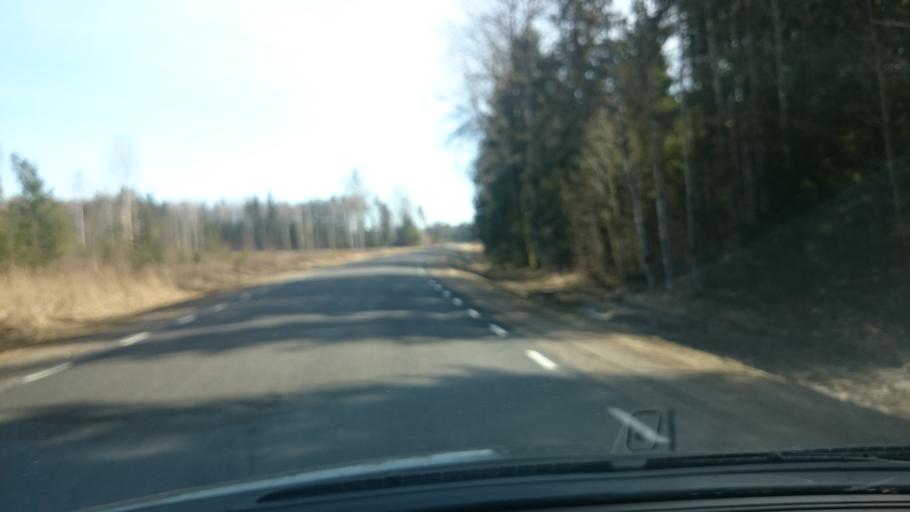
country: EE
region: Paernumaa
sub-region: Tootsi vald
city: Tootsi
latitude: 58.6439
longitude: 24.8822
